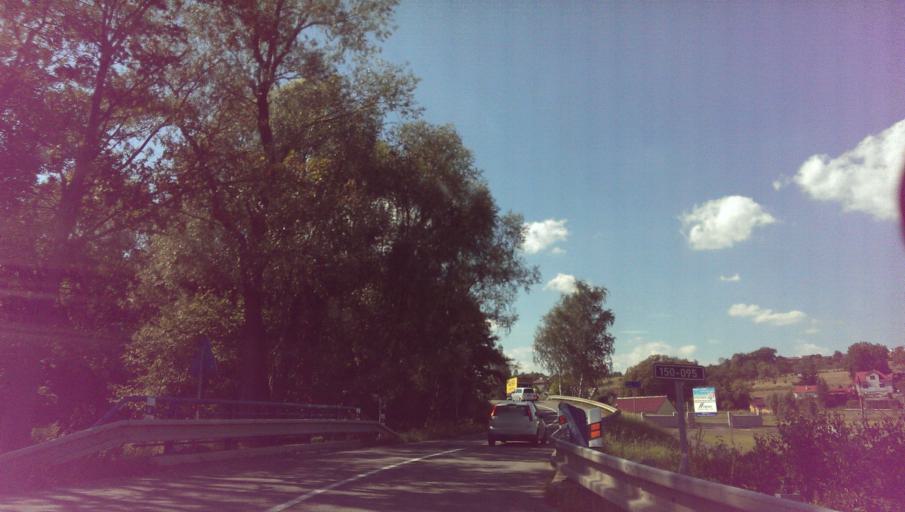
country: CZ
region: Zlin
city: Kelc
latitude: 49.4490
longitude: 17.8702
